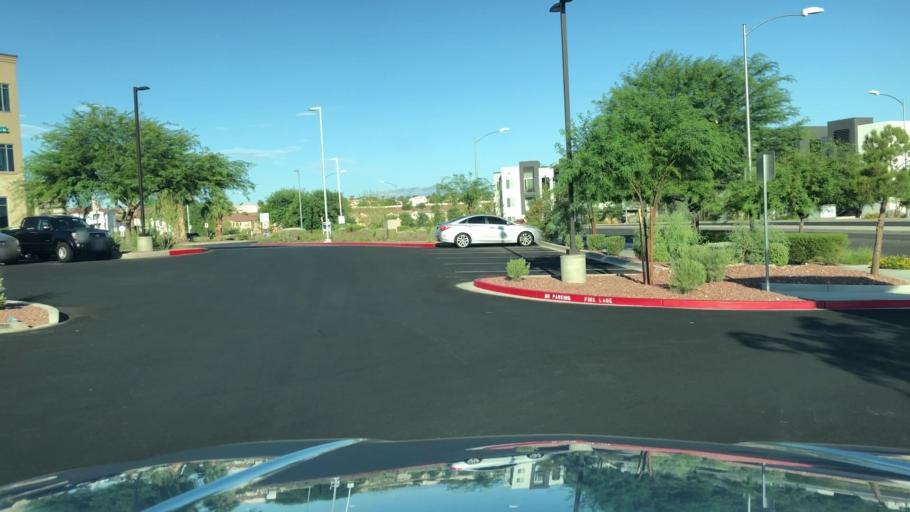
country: US
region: Nevada
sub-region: Clark County
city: Whitney
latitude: 36.0341
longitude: -115.0483
